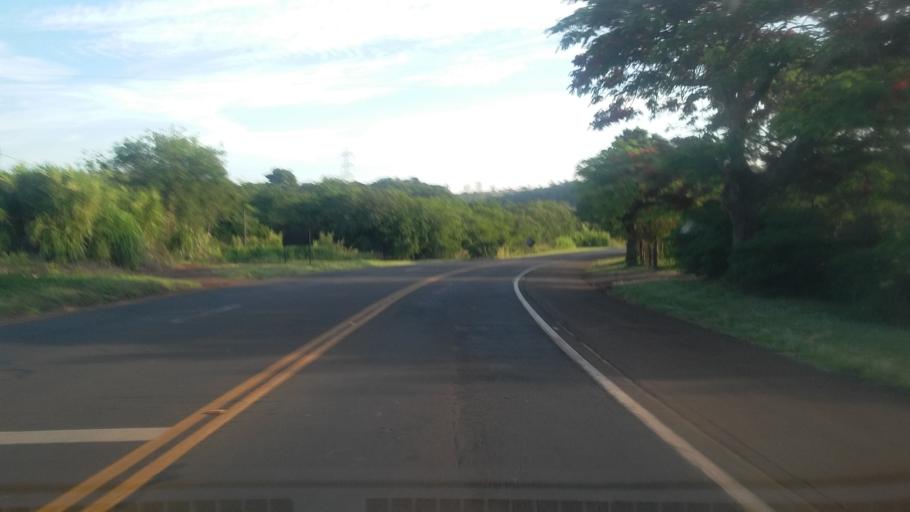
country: BR
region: Parana
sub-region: Assai
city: Assai
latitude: -23.2137
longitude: -50.6689
